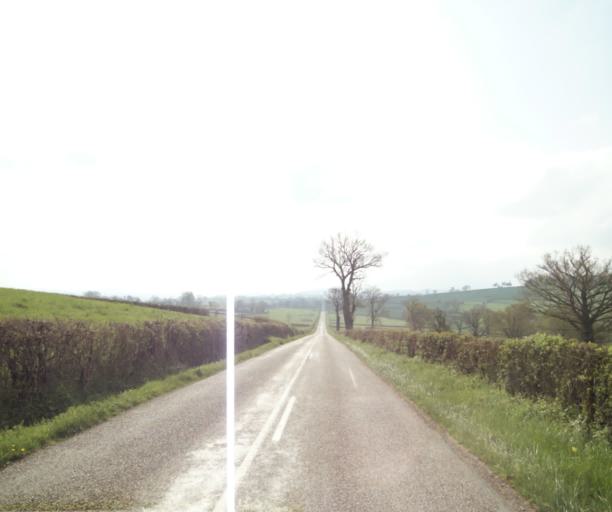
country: FR
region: Bourgogne
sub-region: Departement de Saone-et-Loire
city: Charolles
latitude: 46.3909
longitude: 4.2376
